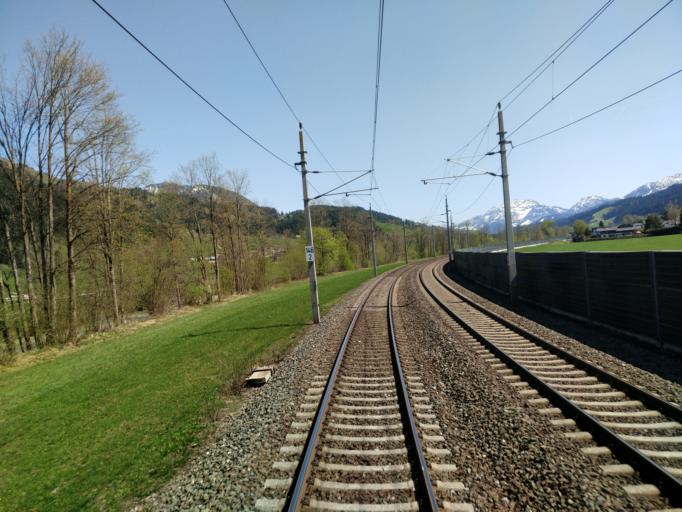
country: AT
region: Tyrol
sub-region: Politischer Bezirk Kitzbuhel
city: Sankt Johann in Tirol
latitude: 47.5176
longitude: 12.4496
